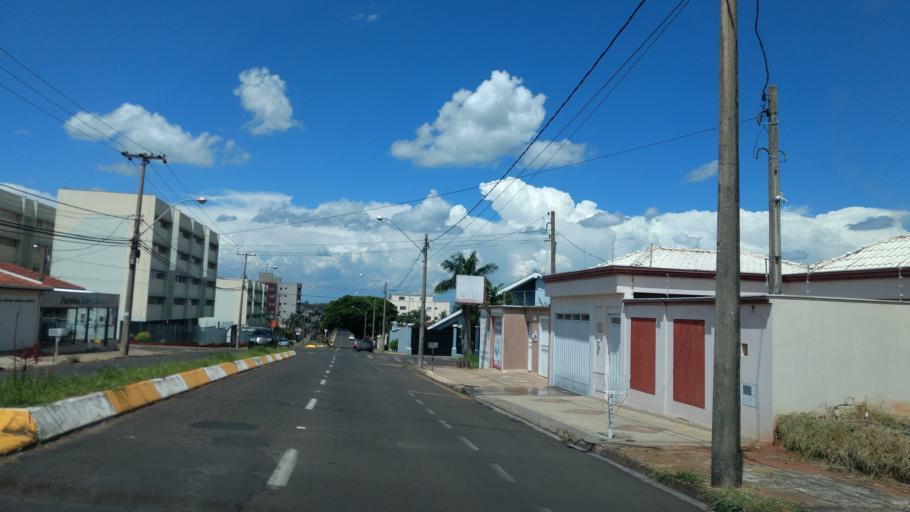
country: BR
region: Sao Paulo
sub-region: Botucatu
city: Botucatu
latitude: -22.8621
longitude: -48.4453
